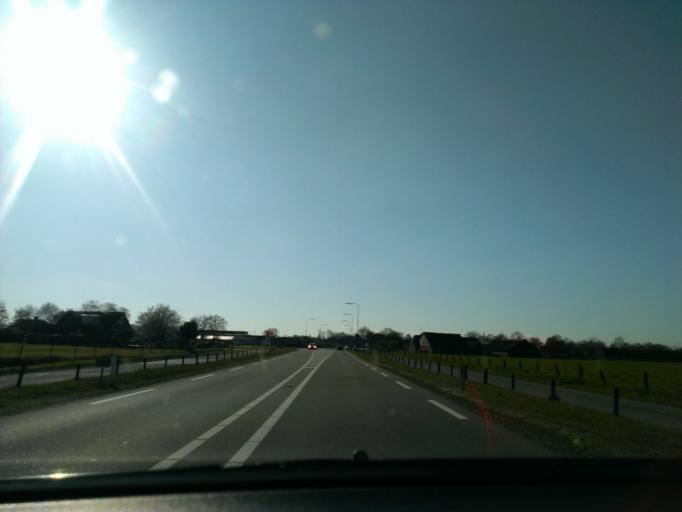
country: NL
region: Overijssel
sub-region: Gemeente Dalfsen
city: Dalfsen
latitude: 52.5303
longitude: 6.3206
